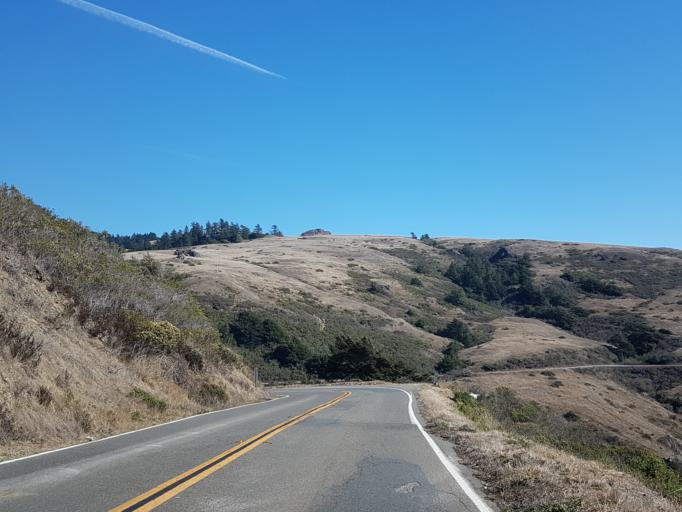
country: US
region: California
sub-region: Sonoma County
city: Monte Rio
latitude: 38.4749
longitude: -123.1556
